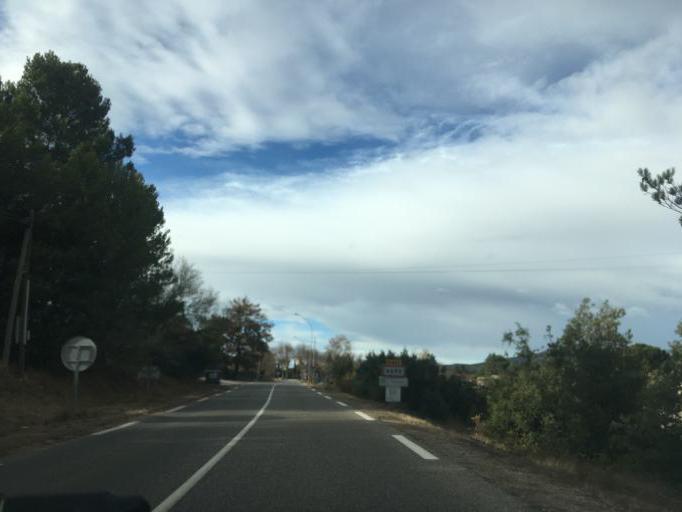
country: FR
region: Provence-Alpes-Cote d'Azur
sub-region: Departement du Var
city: Aups
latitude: 43.6185
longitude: 6.2237
